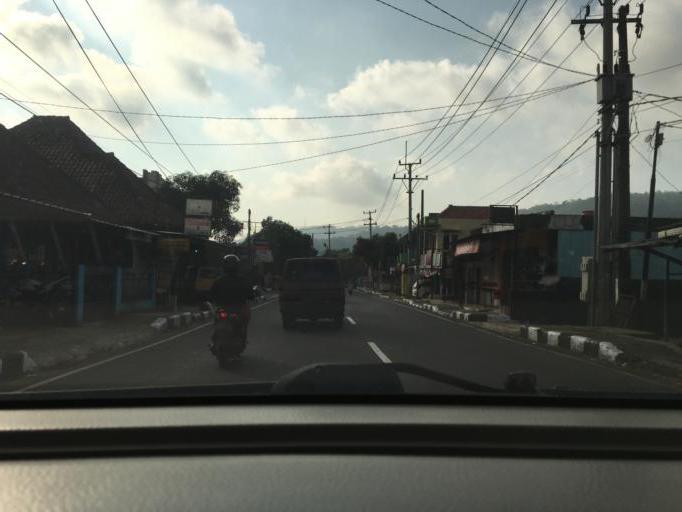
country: ID
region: West Java
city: Kadugede
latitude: -7.0045
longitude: 108.4537
